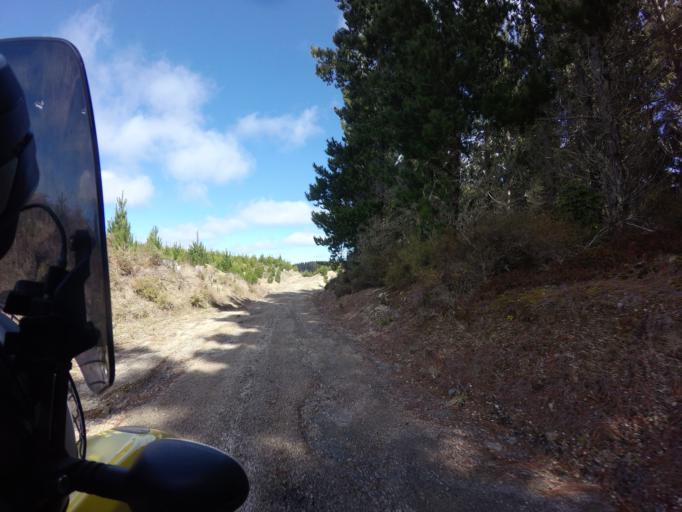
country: NZ
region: Bay of Plenty
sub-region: Whakatane District
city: Murupara
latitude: -38.8200
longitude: 176.5533
